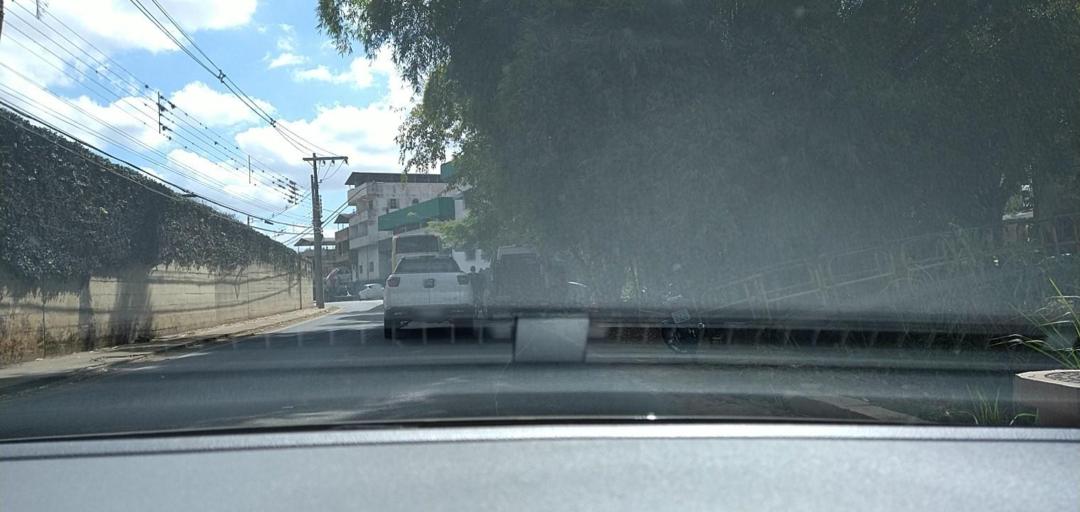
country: BR
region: Minas Gerais
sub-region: Ponte Nova
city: Ponte Nova
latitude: -20.4213
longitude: -42.8986
